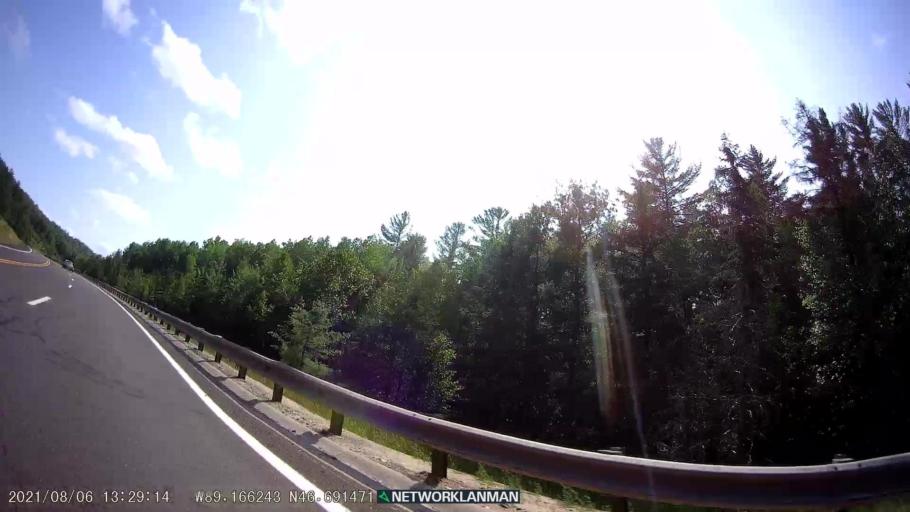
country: US
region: Michigan
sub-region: Ontonagon County
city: Ontonagon
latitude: 46.6909
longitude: -89.1661
